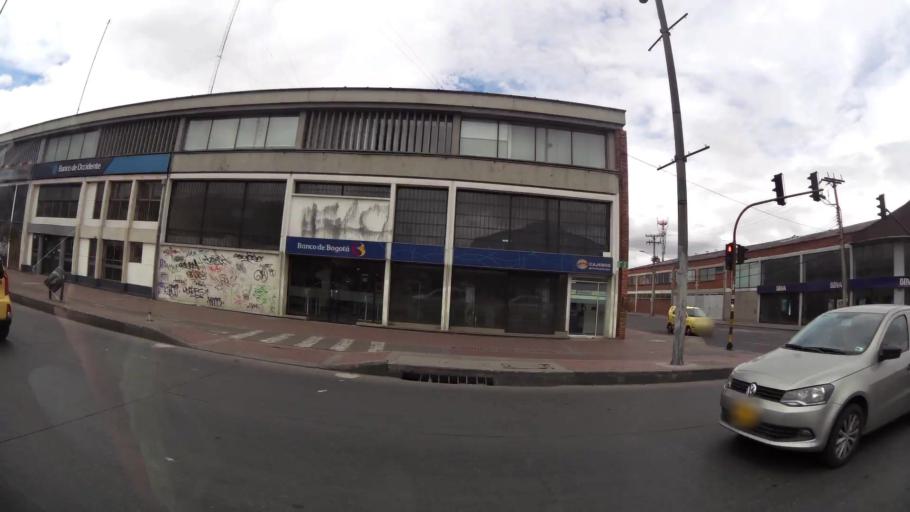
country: CO
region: Bogota D.C.
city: Bogota
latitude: 4.6250
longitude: -74.1041
